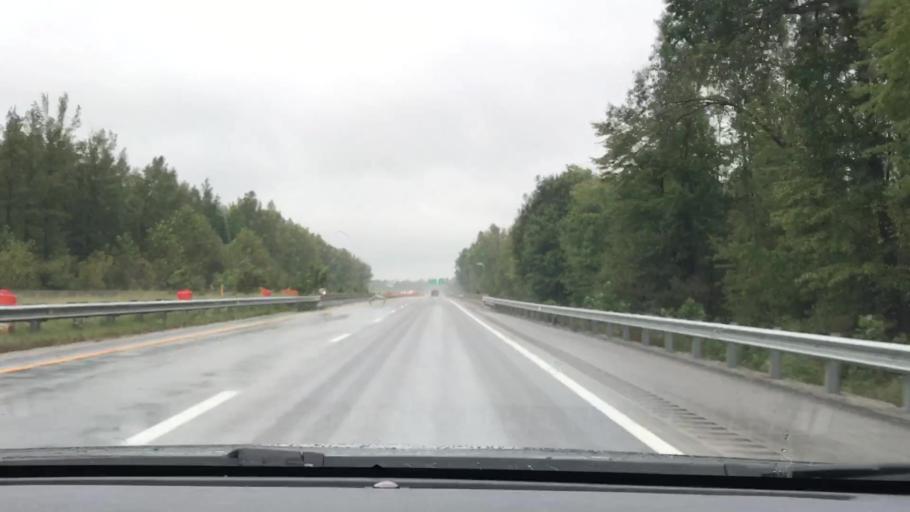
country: US
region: Kentucky
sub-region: Hopkins County
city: Nortonville
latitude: 37.1592
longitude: -87.4591
